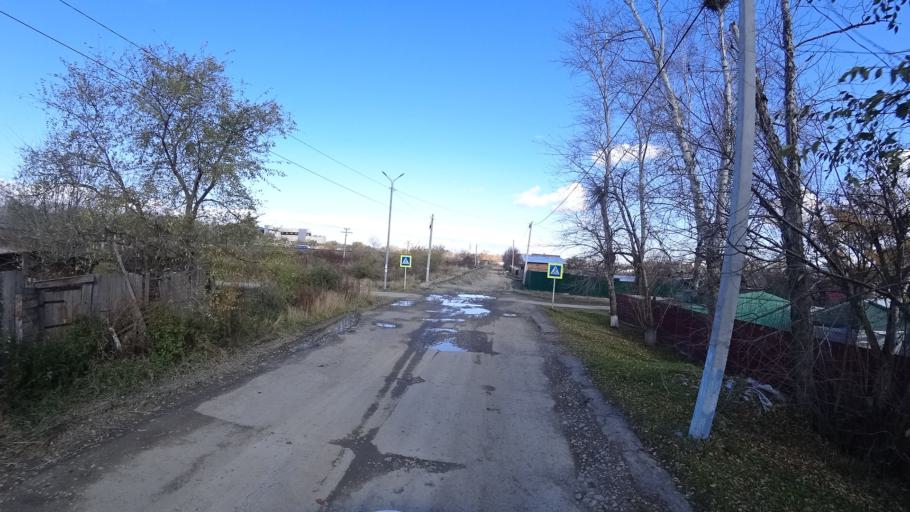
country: RU
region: Khabarovsk Krai
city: Amursk
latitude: 50.1000
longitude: 136.5077
